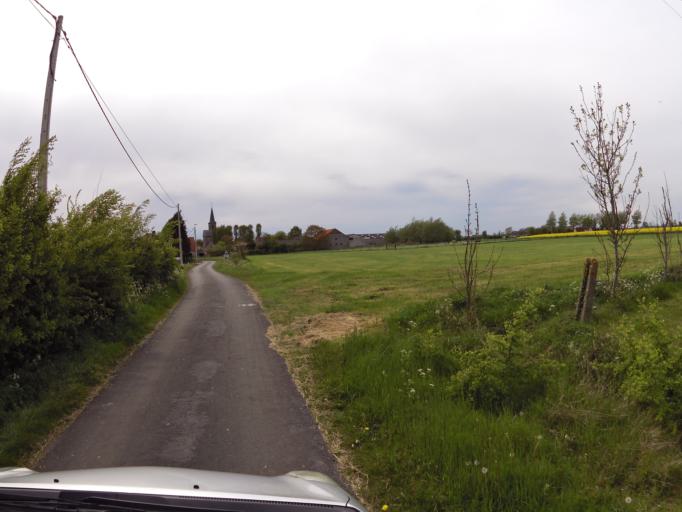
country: BE
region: Flanders
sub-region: Provincie West-Vlaanderen
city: Alveringem
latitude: 51.0510
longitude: 2.7268
